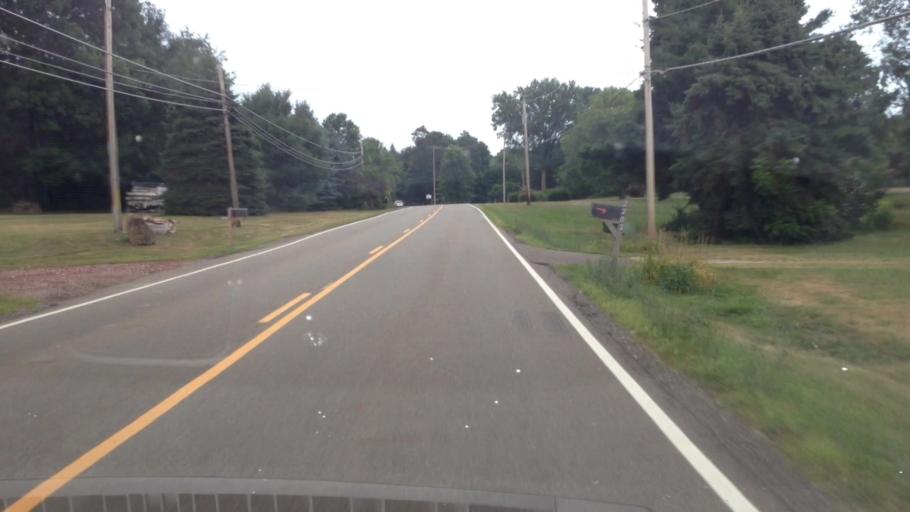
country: US
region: Ohio
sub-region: Summit County
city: Lakemore
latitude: 40.9896
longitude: -81.4564
